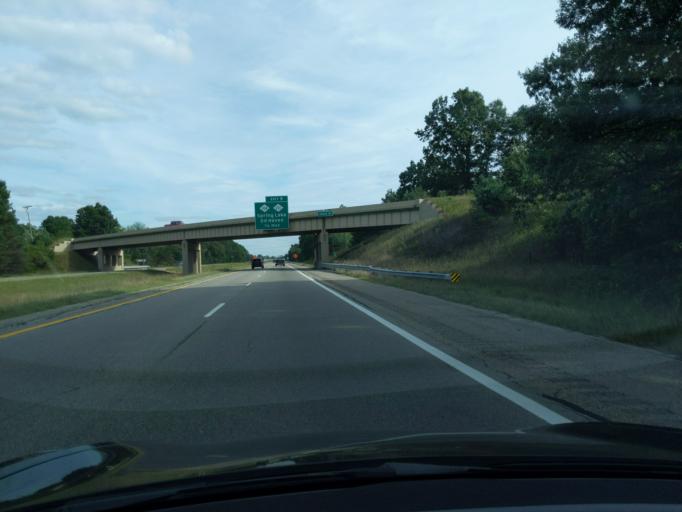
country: US
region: Michigan
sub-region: Muskegon County
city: Fruitport
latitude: 43.0904
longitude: -86.0967
